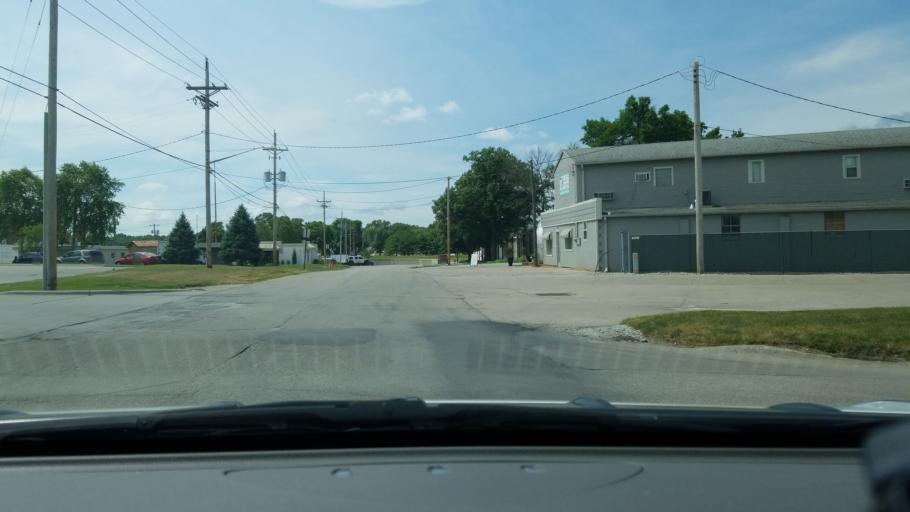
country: US
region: Nebraska
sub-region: Sarpy County
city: Papillion
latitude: 41.1585
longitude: -96.0443
